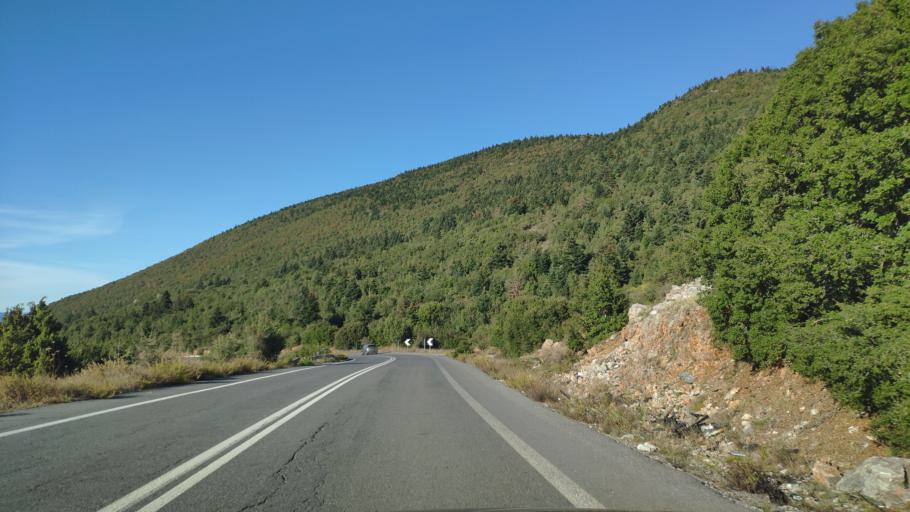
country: GR
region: Peloponnese
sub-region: Nomos Arkadias
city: Langadhia
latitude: 37.6969
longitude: 22.1989
